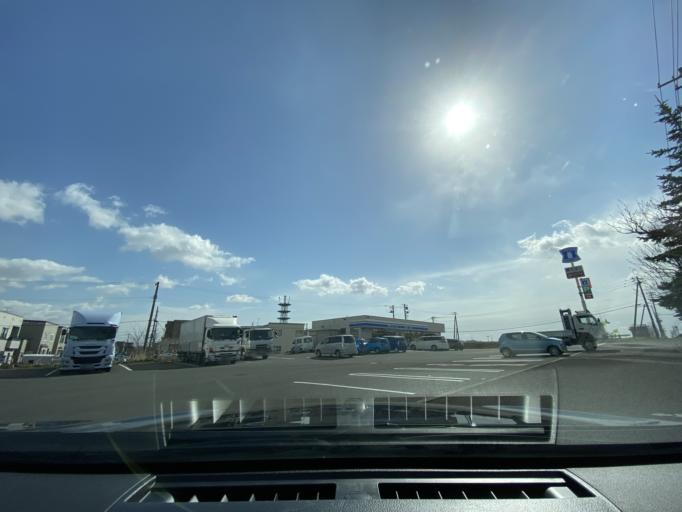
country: JP
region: Hokkaido
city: Kitahiroshima
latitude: 42.9631
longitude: 141.4895
